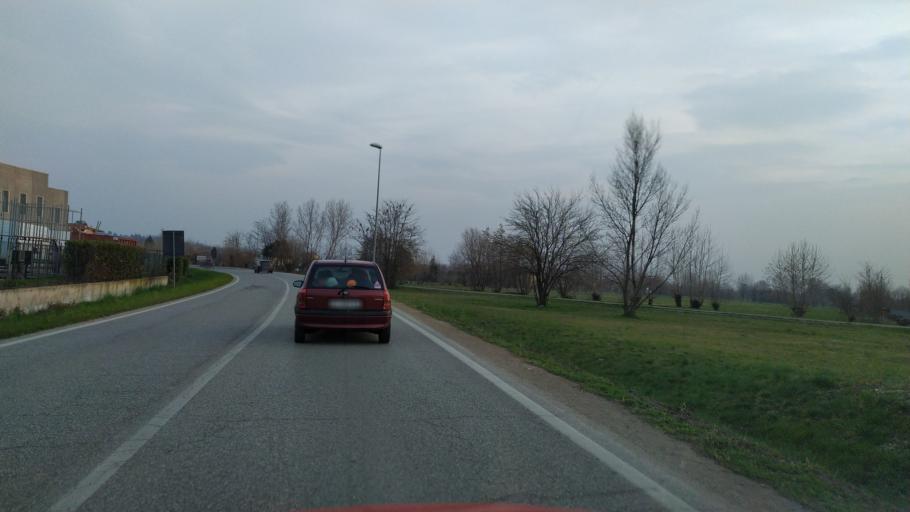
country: IT
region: Veneto
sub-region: Provincia di Vicenza
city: Preara-Moraro-Leva Nord
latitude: 45.6844
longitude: 11.5336
